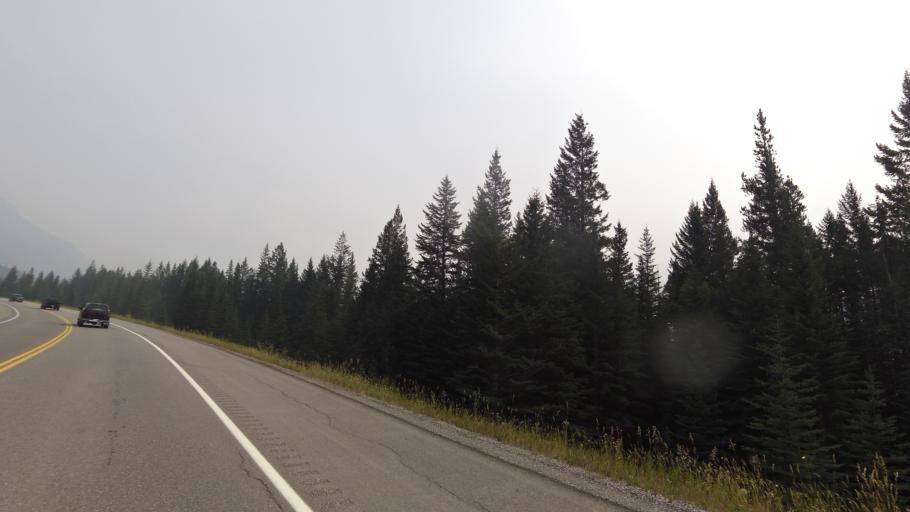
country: CA
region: British Columbia
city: Invermere
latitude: 50.9411
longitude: -115.9875
